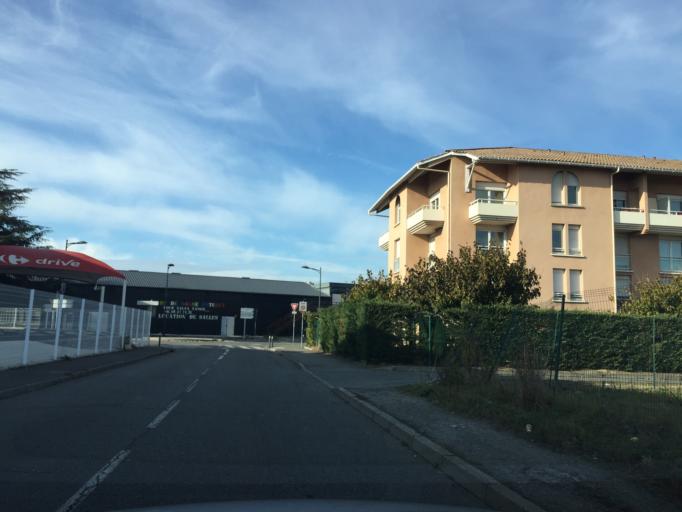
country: FR
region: Midi-Pyrenees
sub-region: Departement de la Haute-Garonne
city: Blagnac
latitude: 43.6113
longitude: 1.3929
